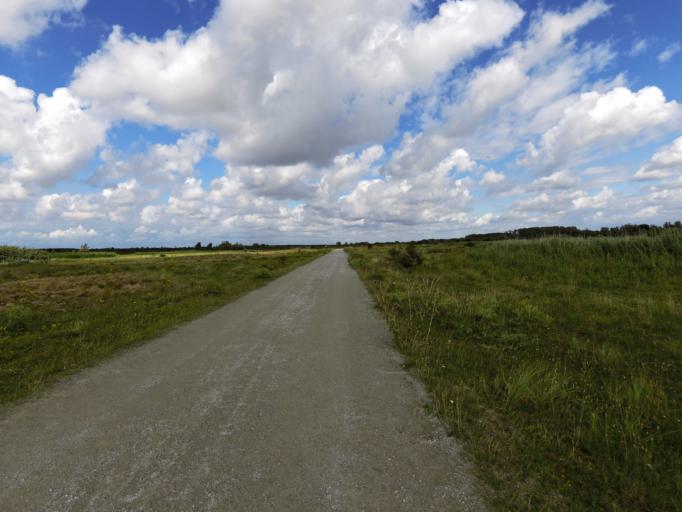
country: NL
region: South Holland
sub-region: Gemeente Goeree-Overflakkee
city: Ouddorp
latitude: 51.8311
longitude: 3.9549
